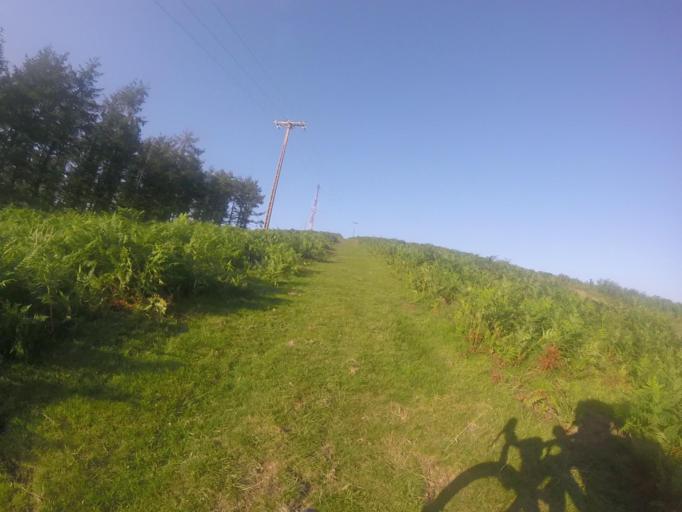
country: ES
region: Navarre
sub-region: Provincia de Navarra
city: Arano
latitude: 43.2438
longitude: -1.8503
